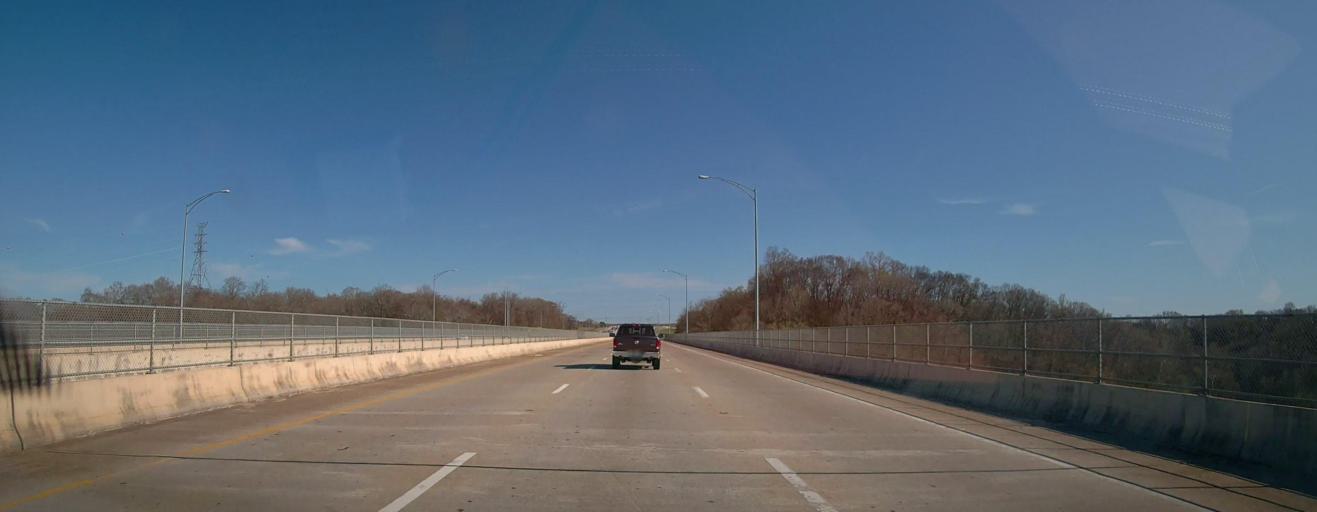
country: US
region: Alabama
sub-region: Lauderdale County
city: East Florence
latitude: 34.7926
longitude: -87.6435
